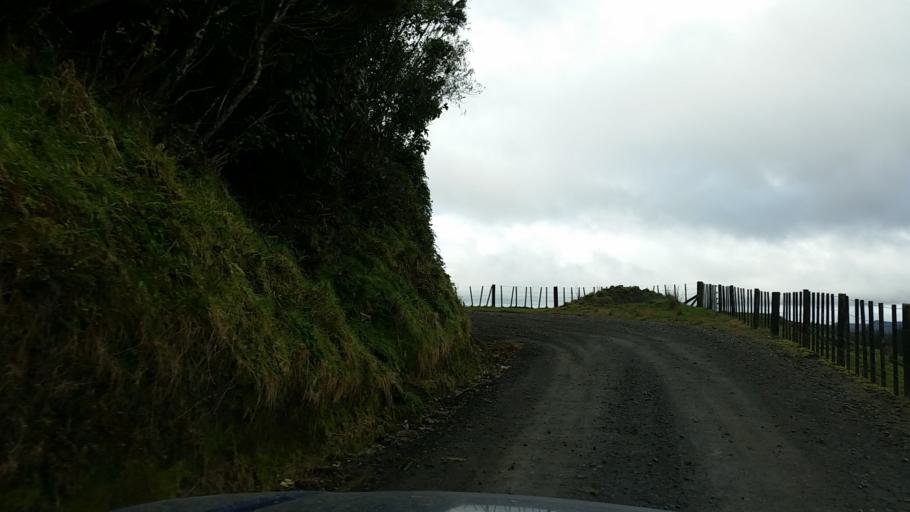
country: NZ
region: Taranaki
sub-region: South Taranaki District
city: Eltham
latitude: -39.1694
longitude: 174.6271
